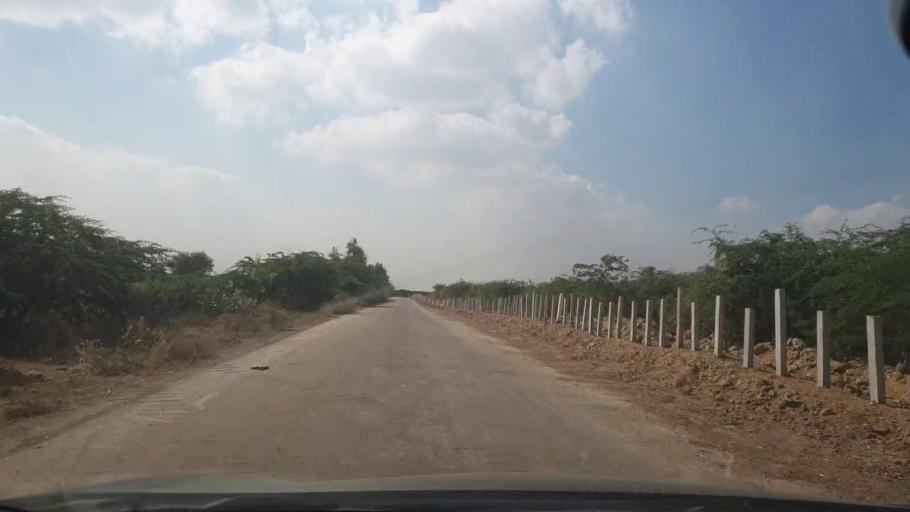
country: PK
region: Sindh
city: Malir Cantonment
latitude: 25.0236
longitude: 67.3574
